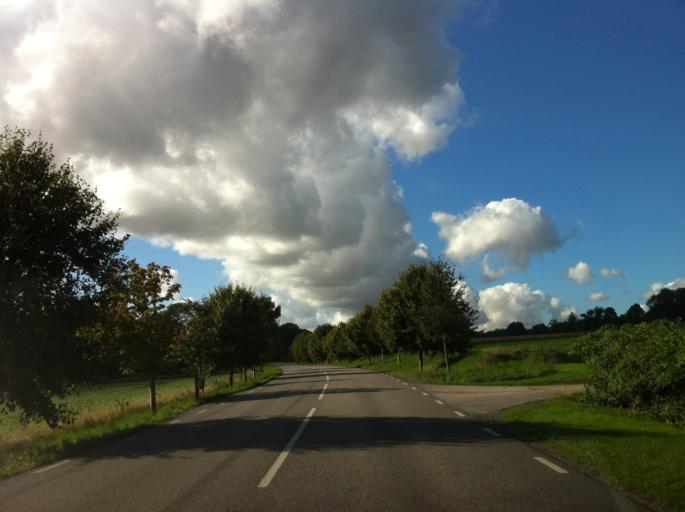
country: SE
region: Skane
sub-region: Eslovs Kommun
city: Eslov
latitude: 55.7786
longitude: 13.2972
